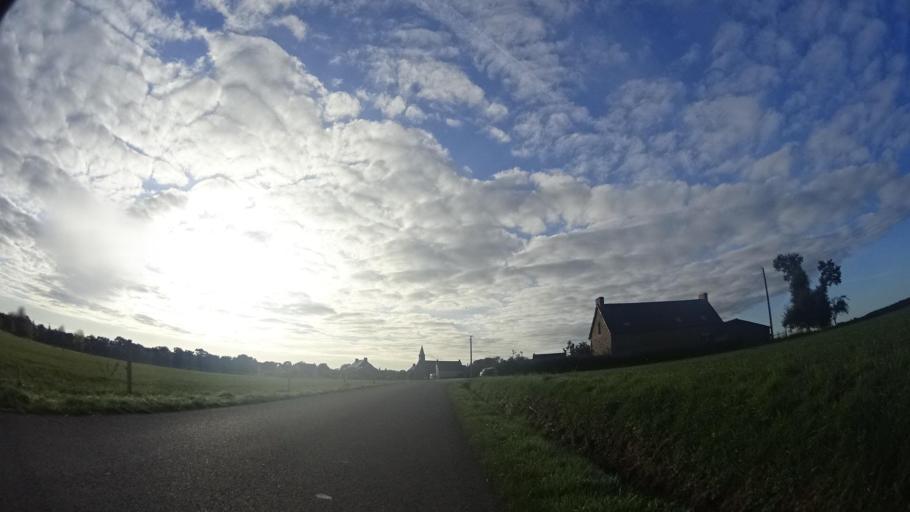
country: FR
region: Brittany
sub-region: Departement des Cotes-d'Armor
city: Evran
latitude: 48.3655
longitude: -1.9559
